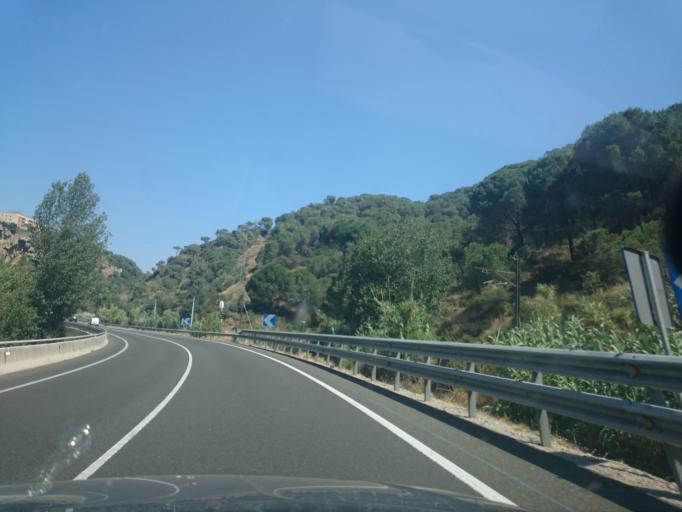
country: ES
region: Catalonia
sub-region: Provincia de Barcelona
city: Capellades
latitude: 41.5256
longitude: 1.6935
